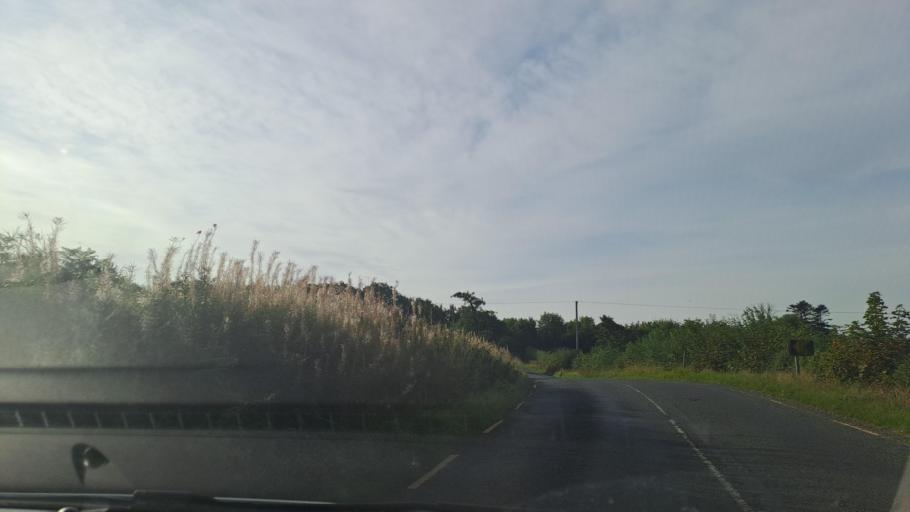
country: IE
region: Ulster
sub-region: An Cabhan
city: Kingscourt
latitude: 53.9234
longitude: -6.8138
